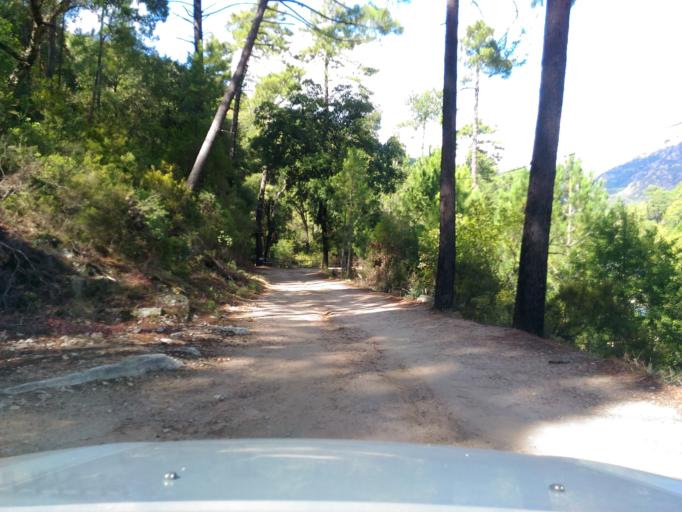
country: FR
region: Corsica
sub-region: Departement de la Corse-du-Sud
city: Porto-Vecchio
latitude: 41.7186
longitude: 9.3024
